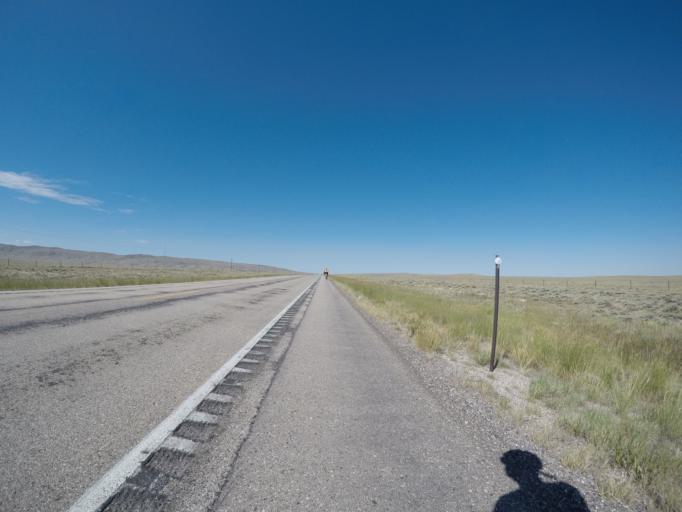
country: US
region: Wyoming
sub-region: Carbon County
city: Saratoga
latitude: 41.8112
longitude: -106.6801
